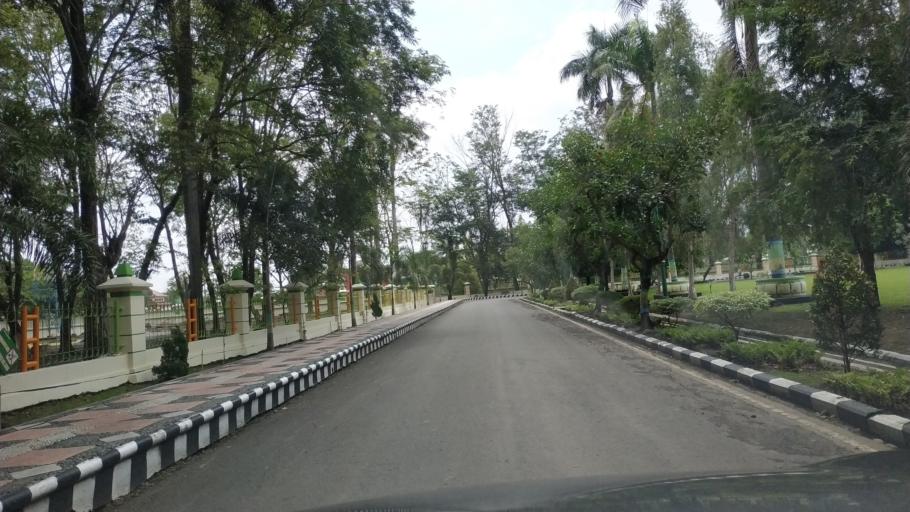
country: ID
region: Central Java
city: Slawi
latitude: -6.9948
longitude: 109.1273
